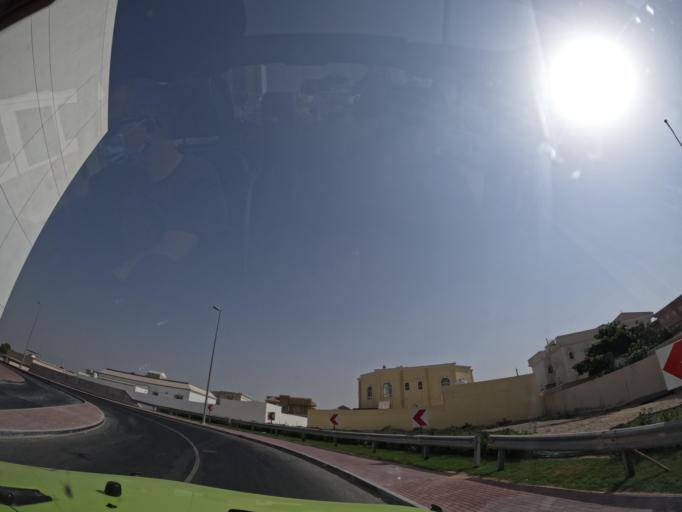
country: AE
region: Ash Shariqah
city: Sharjah
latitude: 25.2056
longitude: 55.4263
